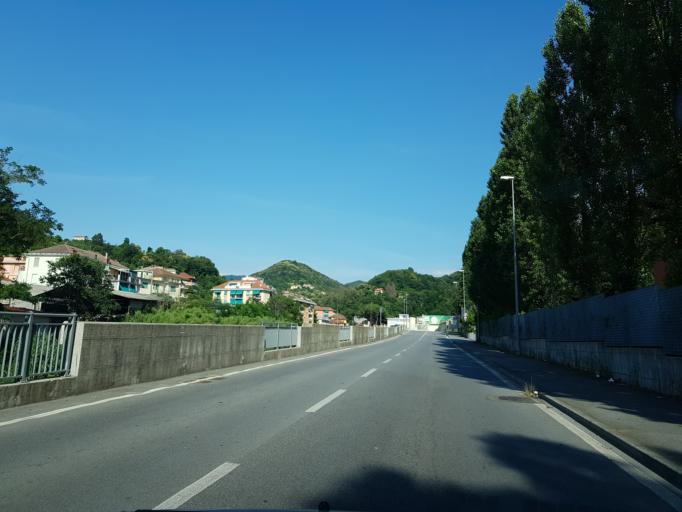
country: IT
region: Liguria
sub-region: Provincia di Genova
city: Manesseno
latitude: 44.4768
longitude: 8.9230
